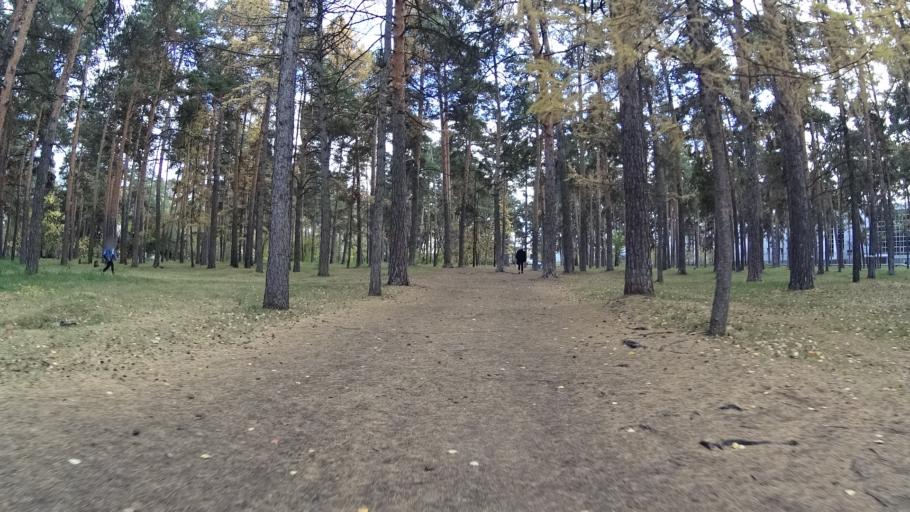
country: RU
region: Chelyabinsk
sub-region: Gorod Chelyabinsk
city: Chelyabinsk
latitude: 55.1621
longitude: 61.3641
